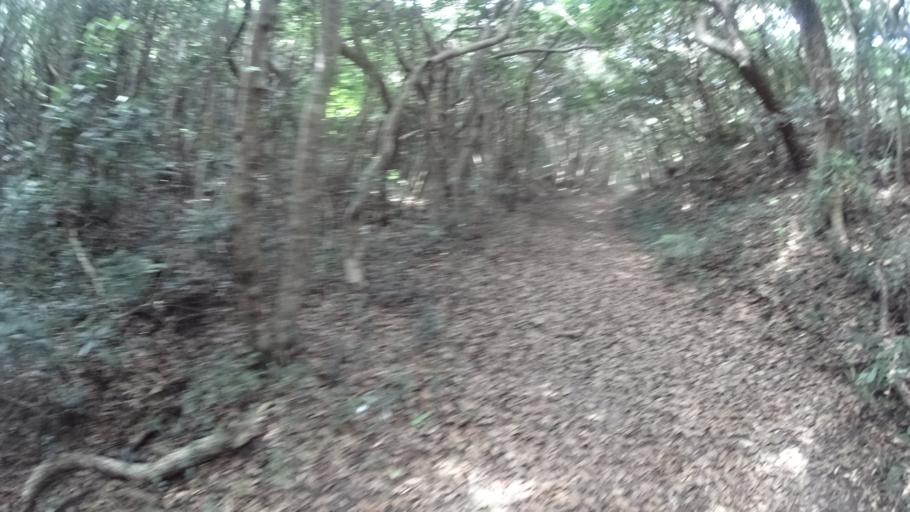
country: JP
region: Shizuoka
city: Shimoda
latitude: 34.3209
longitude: 139.2018
